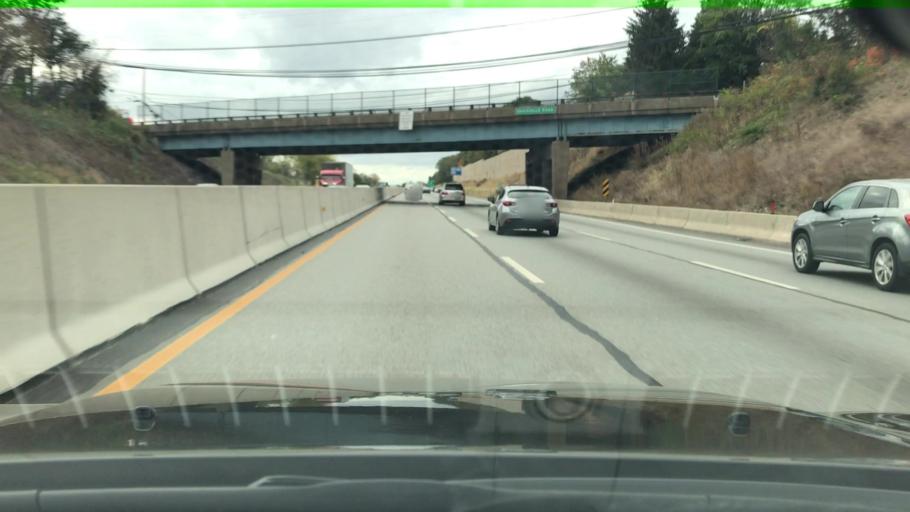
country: US
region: Pennsylvania
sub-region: Montgomery County
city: Hatboro
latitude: 40.1628
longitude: -75.0899
